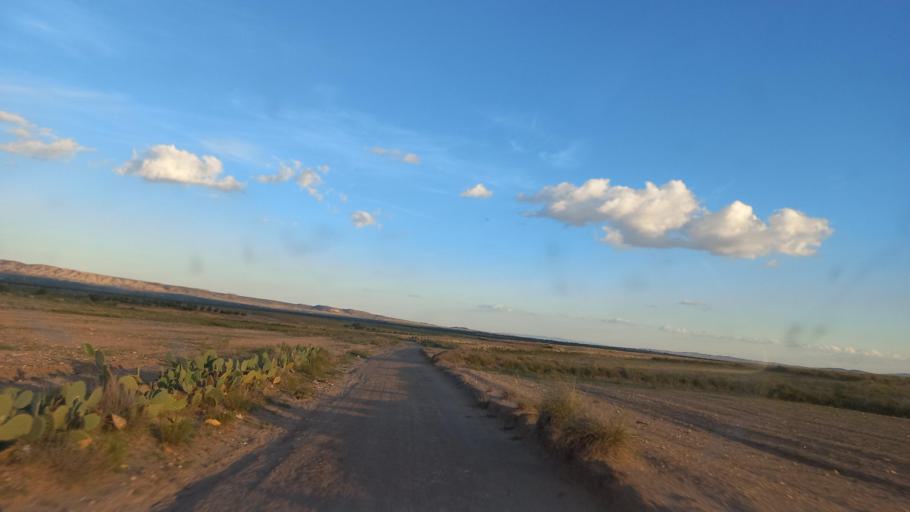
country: TN
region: Al Qasrayn
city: Sbiba
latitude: 35.3503
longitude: 9.0222
